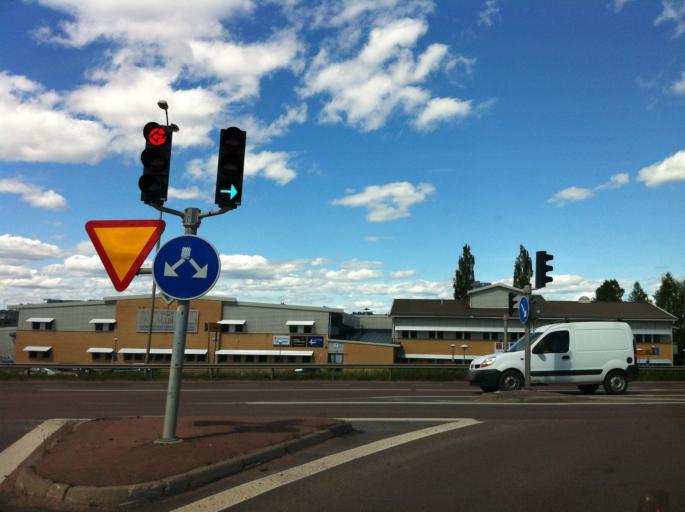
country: SE
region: Dalarna
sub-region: Mora Kommun
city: Mora
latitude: 61.0091
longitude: 14.5663
